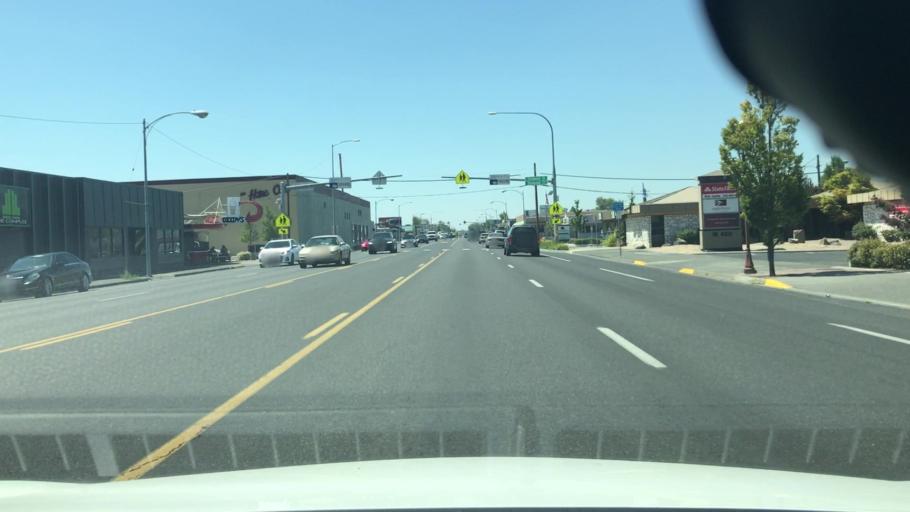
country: US
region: Washington
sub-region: Grant County
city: Moses Lake
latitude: 47.1290
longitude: -119.2831
